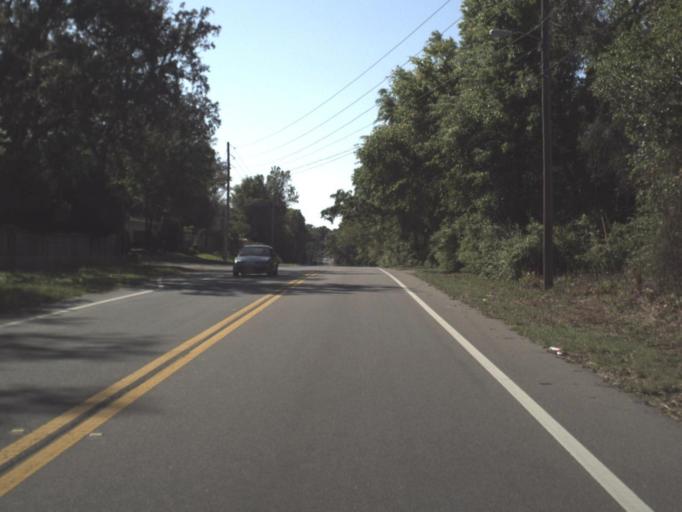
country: US
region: Florida
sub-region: Escambia County
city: Ferry Pass
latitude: 30.5186
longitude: -87.1697
